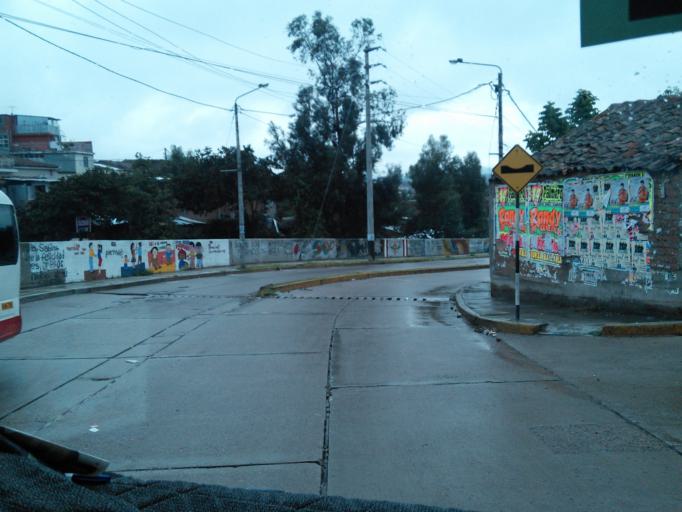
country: PE
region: Ayacucho
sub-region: Provincia de Huamanga
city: Ayacucho
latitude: -13.1689
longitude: -74.2269
